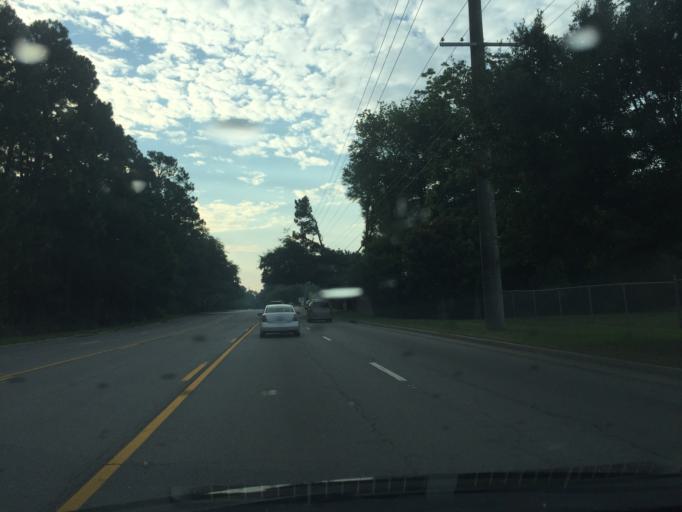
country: US
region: Georgia
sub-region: Chatham County
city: Isle of Hope
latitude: 31.9922
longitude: -81.0981
